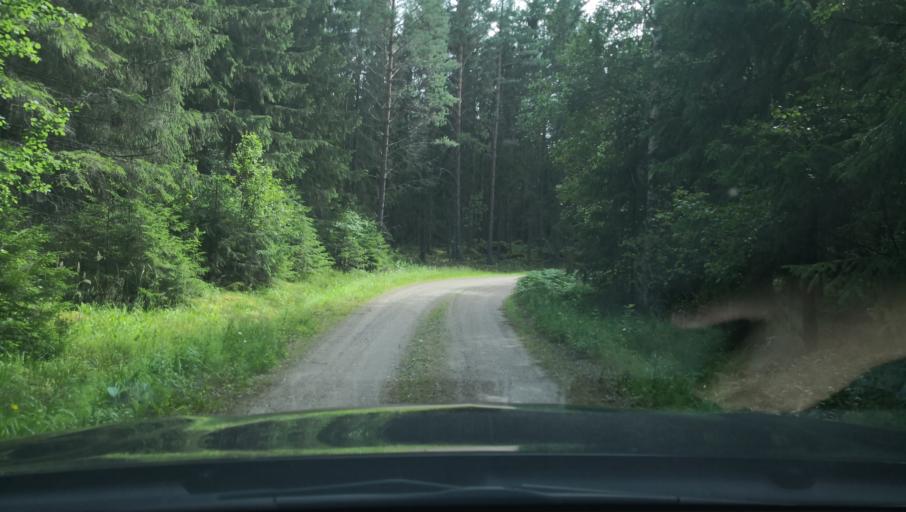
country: SE
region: Vaestmanland
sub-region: Hallstahammars Kommun
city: Hallstahammar
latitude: 59.6503
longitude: 16.1119
